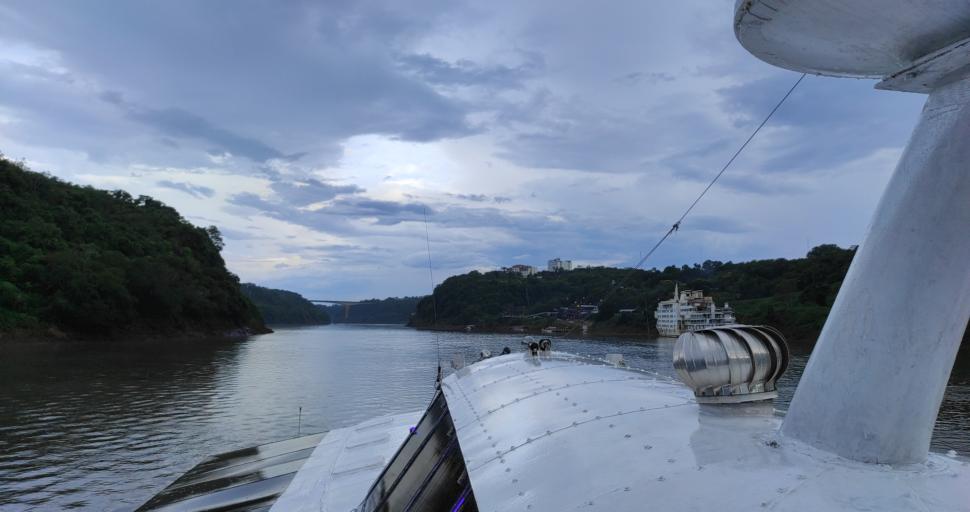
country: AR
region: Misiones
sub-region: Departamento de Iguazu
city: Puerto Iguazu
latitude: -25.5926
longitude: -54.5857
